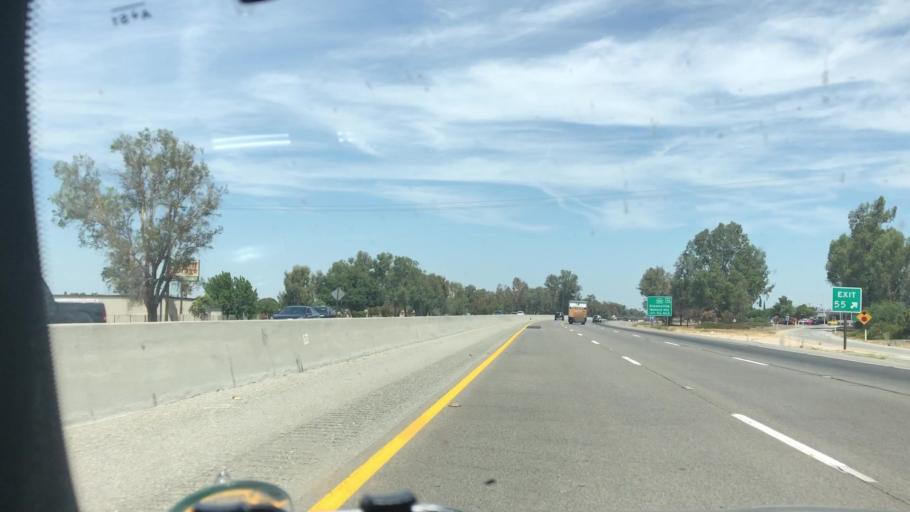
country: US
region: California
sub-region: Kern County
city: Delano
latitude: 35.7552
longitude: -119.2473
